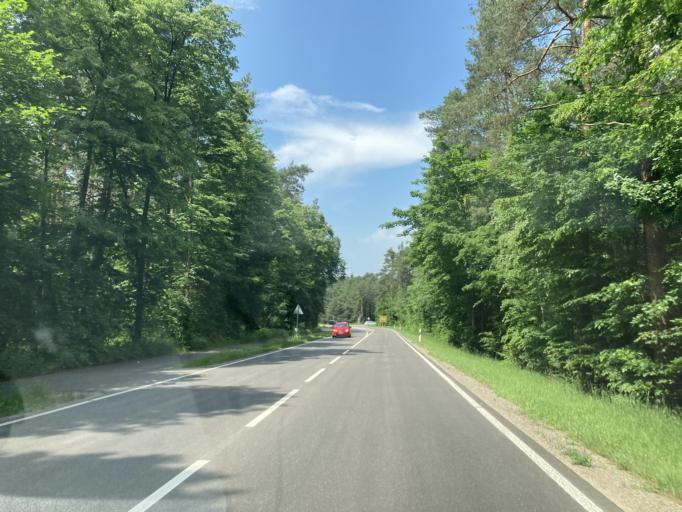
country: DE
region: Baden-Wuerttemberg
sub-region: Karlsruhe Region
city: Eggenstein-Leopoldshafen
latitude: 49.0894
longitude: 8.4487
